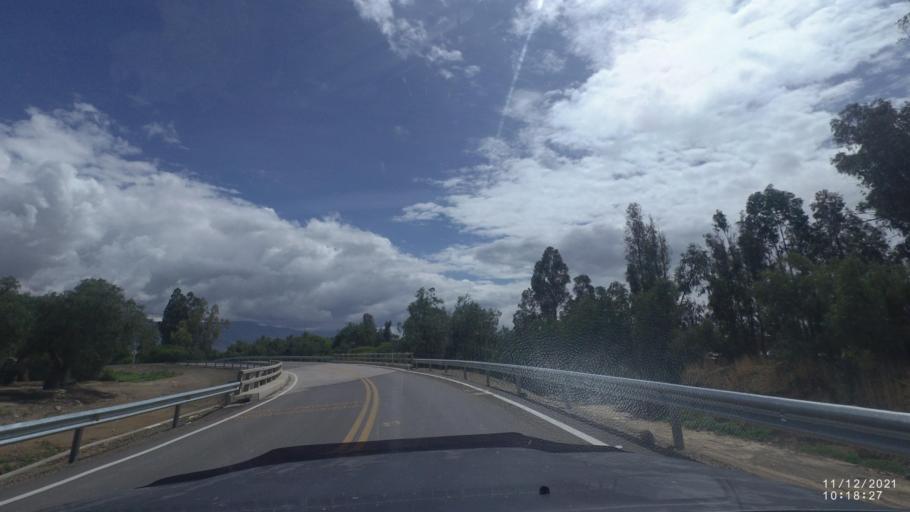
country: BO
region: Cochabamba
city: Tarata
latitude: -17.5797
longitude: -66.0148
